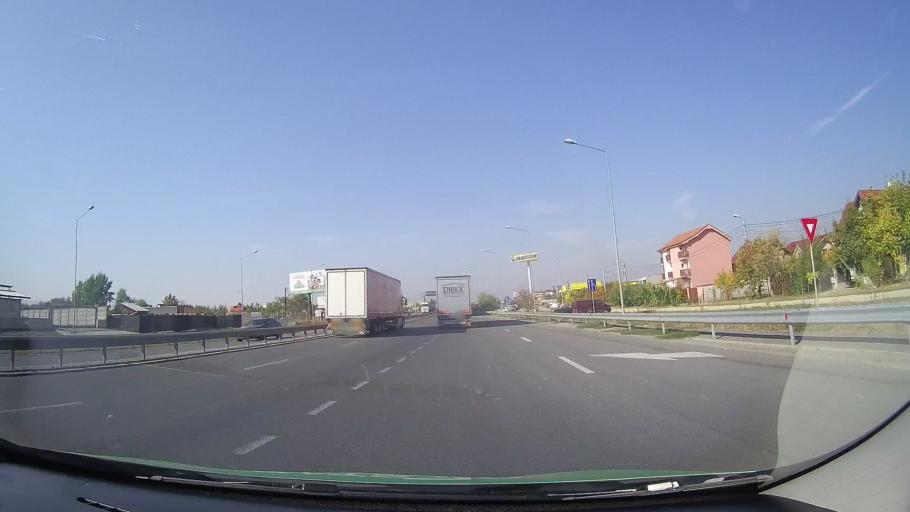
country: RO
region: Bihor
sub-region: Comuna Biharea
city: Oradea
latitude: 47.0469
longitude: 21.8990
